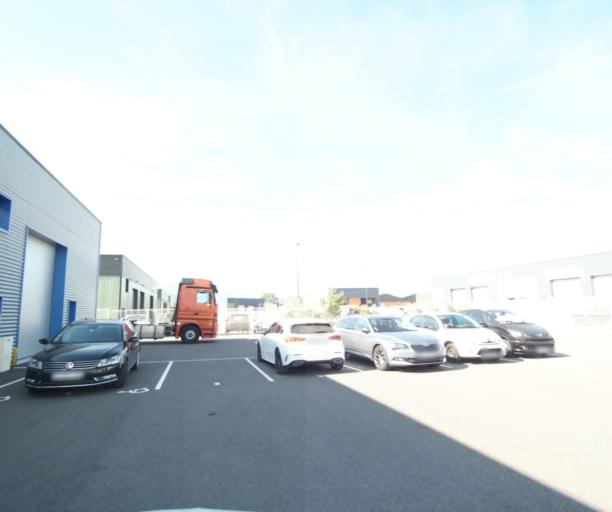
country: FR
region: Rhone-Alpes
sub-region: Departement de la Haute-Savoie
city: Marin
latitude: 46.3919
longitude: 6.5089
